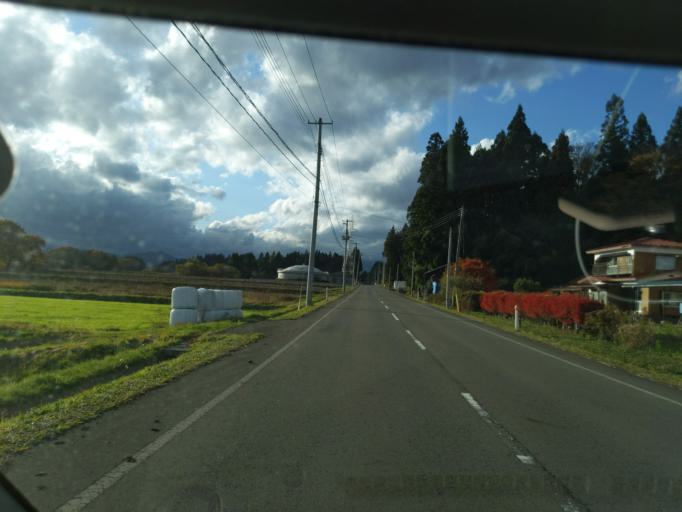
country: JP
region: Iwate
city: Mizusawa
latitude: 39.1084
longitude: 141.0100
